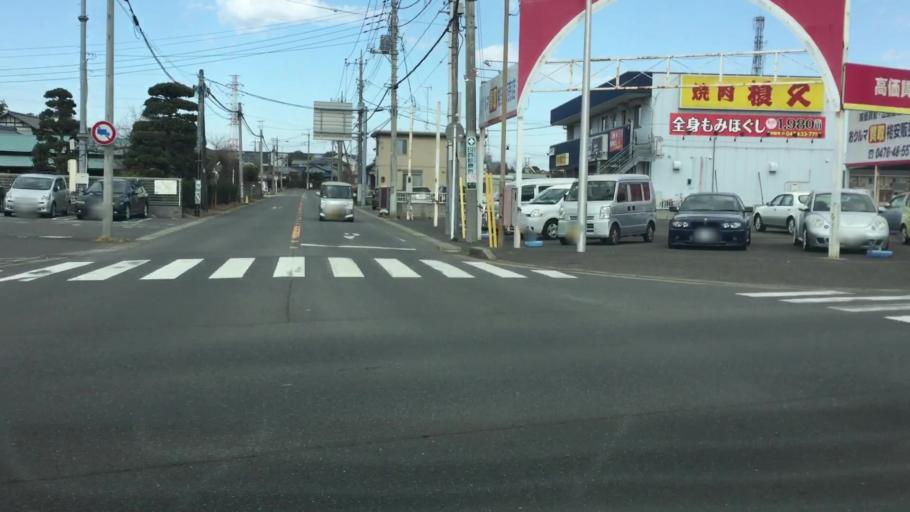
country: JP
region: Chiba
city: Shiroi
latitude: 35.8050
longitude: 140.1347
